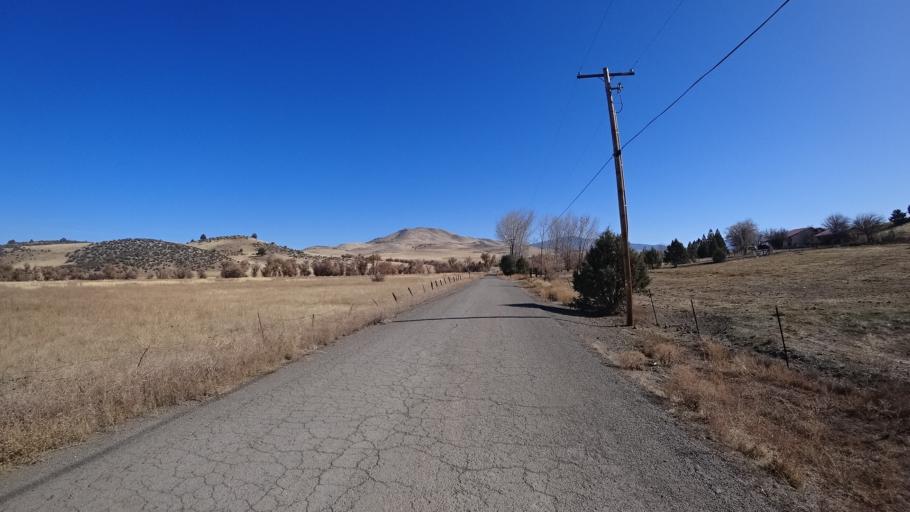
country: US
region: California
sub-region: Siskiyou County
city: Montague
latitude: 41.8478
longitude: -122.4593
